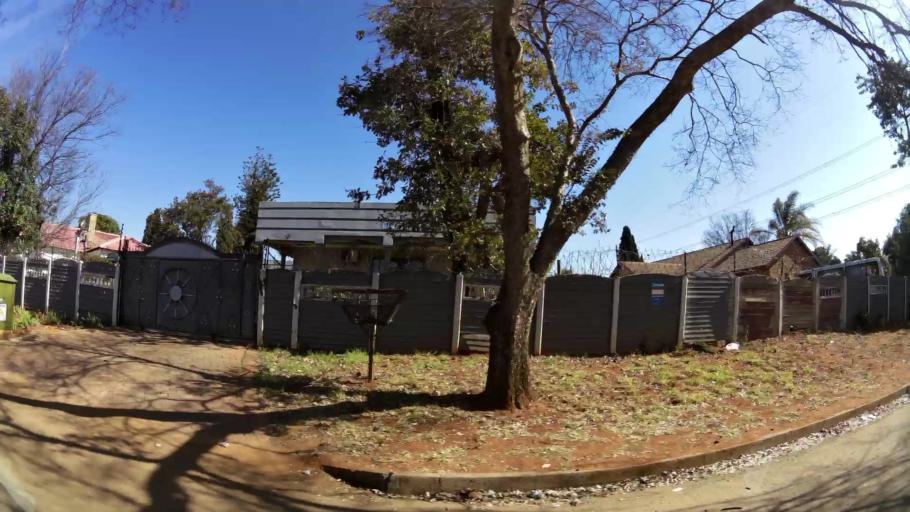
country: ZA
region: Gauteng
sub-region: City of Johannesburg Metropolitan Municipality
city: Modderfontein
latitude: -26.0661
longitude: 28.2119
